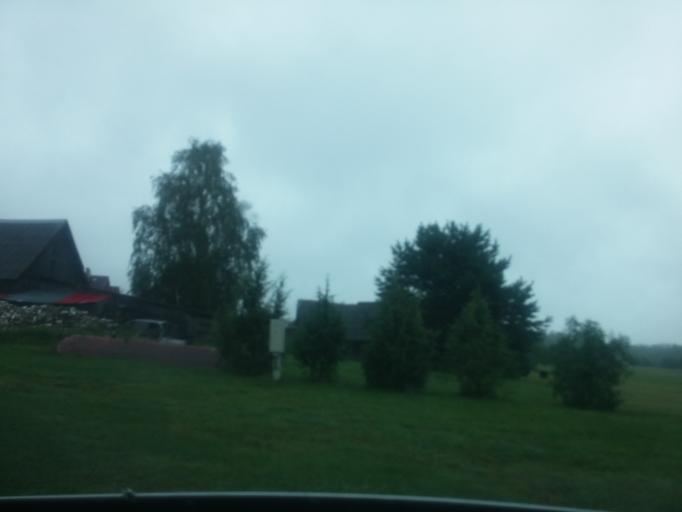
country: LV
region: Ogre
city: Ogre
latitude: 56.8631
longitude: 24.5828
